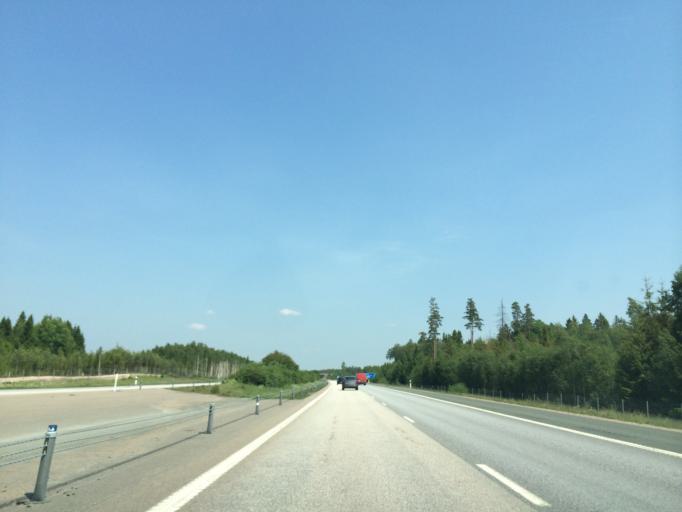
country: SE
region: Kronoberg
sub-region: Ljungby Kommun
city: Lagan
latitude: 57.0316
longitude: 14.0491
